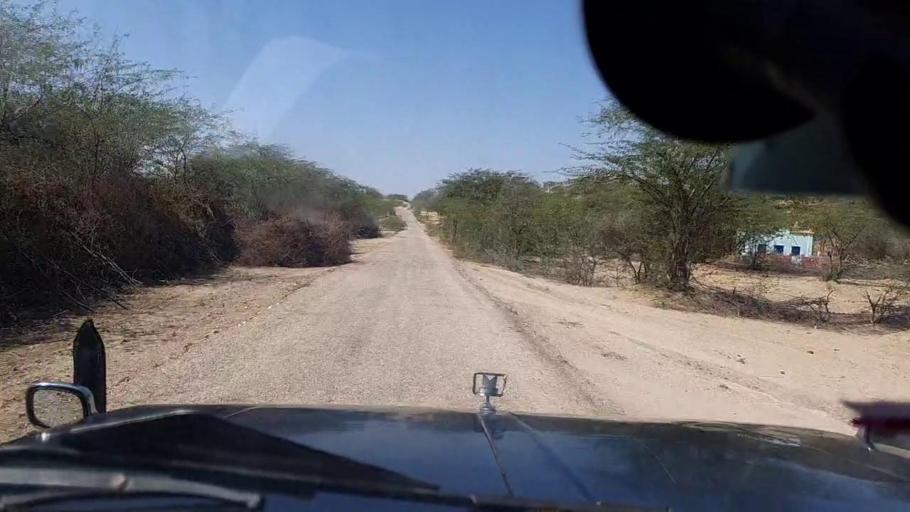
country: PK
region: Sindh
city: Mithi
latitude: 24.6134
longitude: 69.6859
